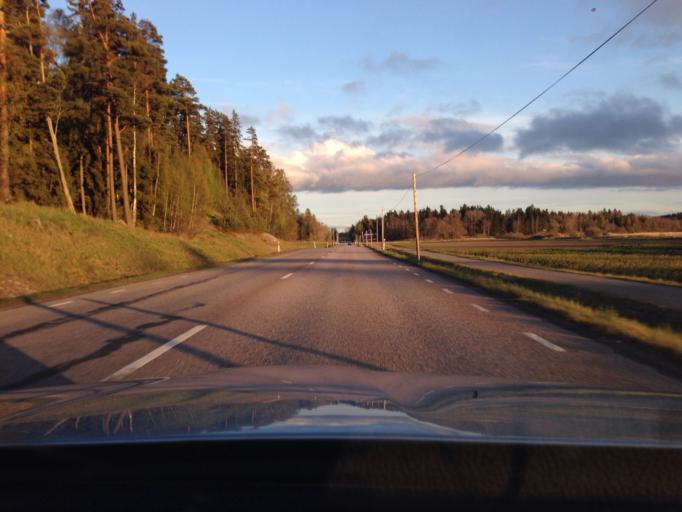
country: SE
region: Soedermanland
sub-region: Trosa Kommun
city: Trosa
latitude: 58.9188
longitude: 17.5428
